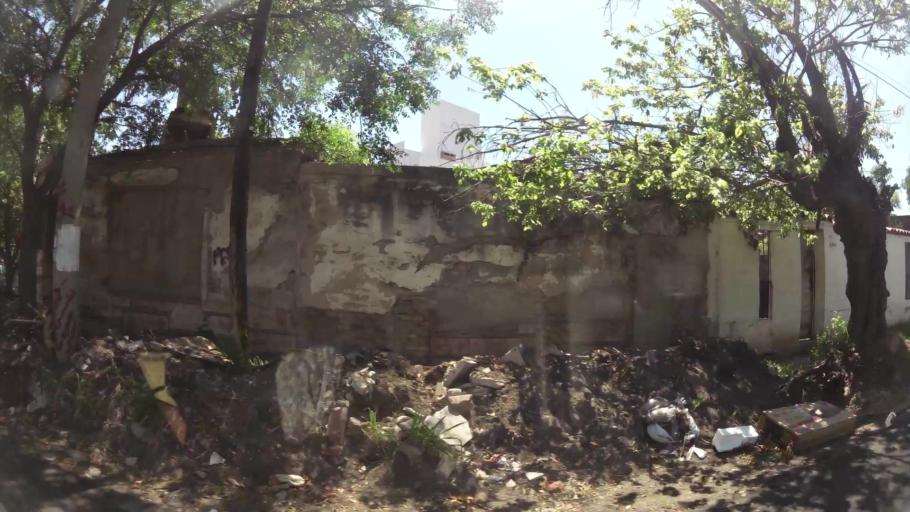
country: AR
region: Cordoba
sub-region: Departamento de Capital
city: Cordoba
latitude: -31.3941
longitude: -64.1934
